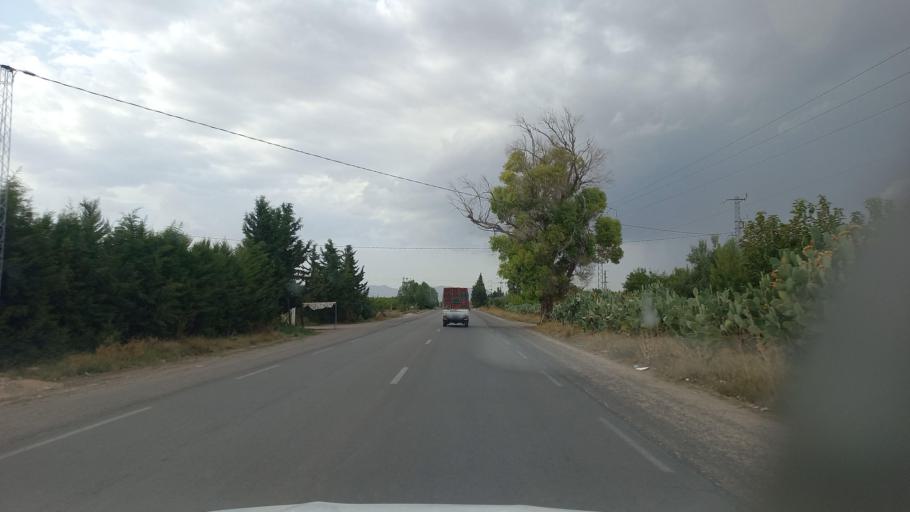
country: TN
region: Al Qasrayn
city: Sbiba
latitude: 35.2988
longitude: 9.0890
